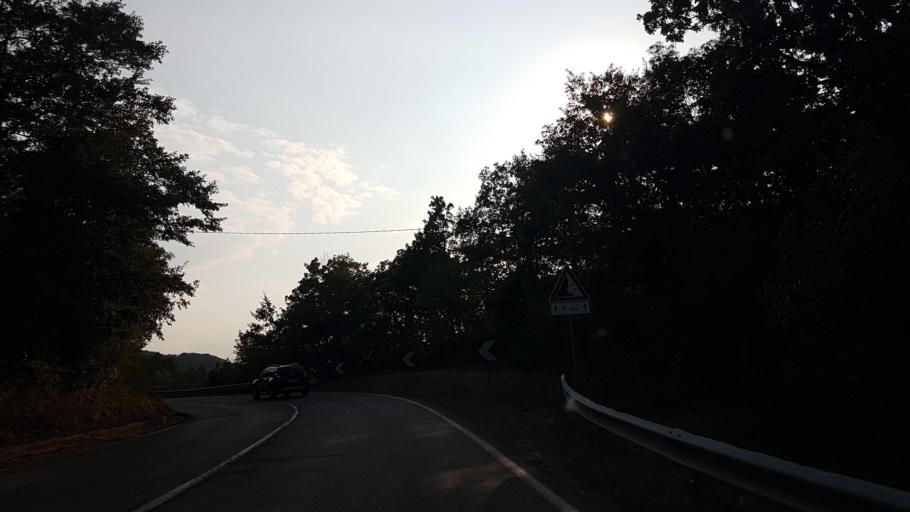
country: IT
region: Emilia-Romagna
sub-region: Provincia di Parma
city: Solignano
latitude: 44.6212
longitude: 10.0024
